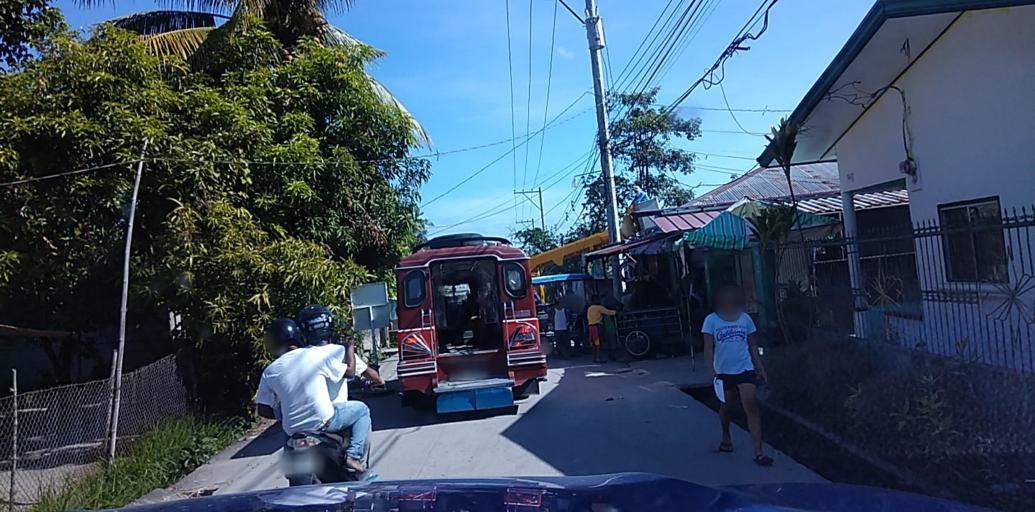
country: PH
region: Central Luzon
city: Santol
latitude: 15.1677
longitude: 120.5070
